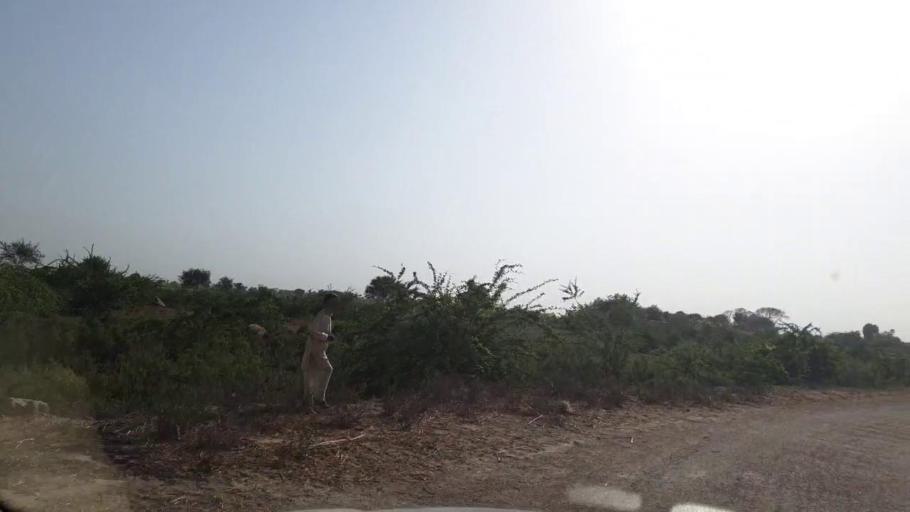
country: PK
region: Sindh
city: Tando Ghulam Ali
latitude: 25.0850
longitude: 68.8527
